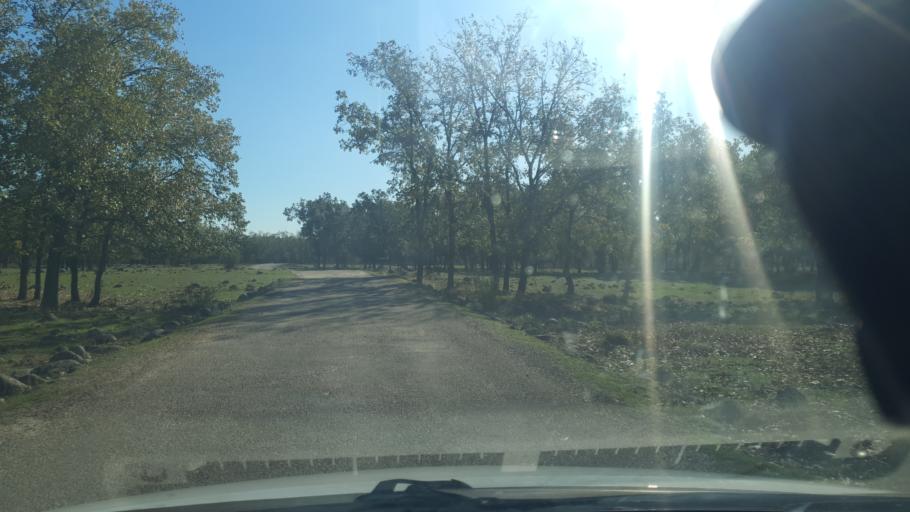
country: ES
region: Castille and Leon
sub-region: Provincia de Avila
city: Candeleda
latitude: 40.1208
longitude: -5.2646
